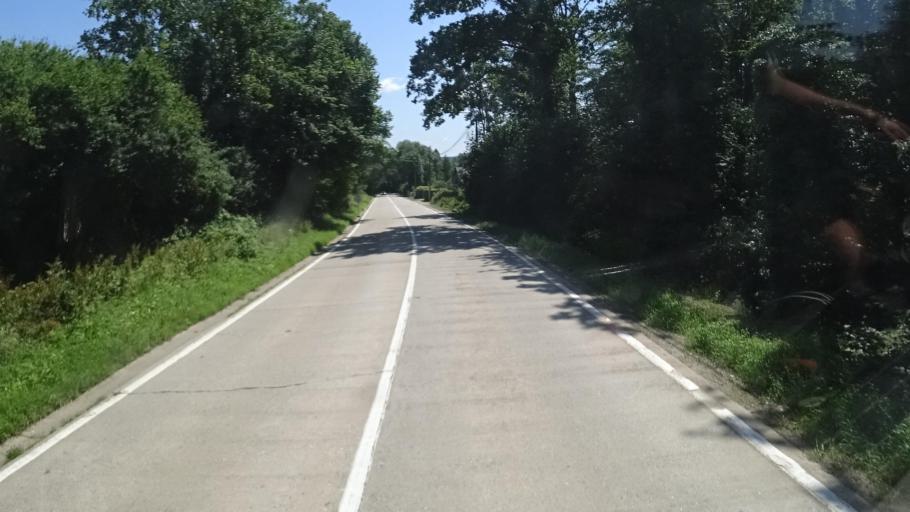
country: BE
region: Wallonia
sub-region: Province de Namur
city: Profondeville
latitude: 50.3816
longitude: 4.8101
